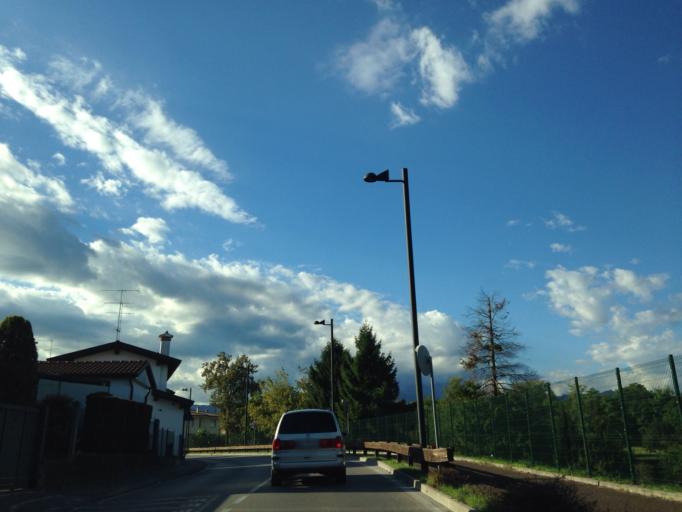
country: IT
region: Friuli Venezia Giulia
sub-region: Provincia di Pordenone
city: Porcia
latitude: 45.9589
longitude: 12.6350
